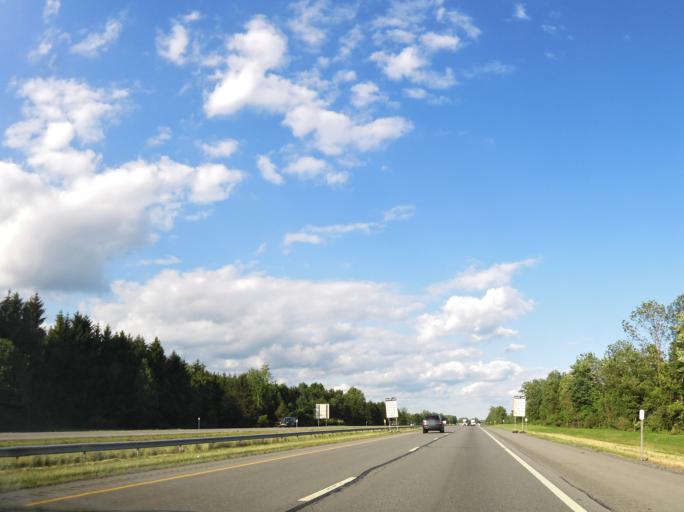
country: US
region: New York
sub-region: Erie County
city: Clarence
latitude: 42.9577
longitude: -78.5809
